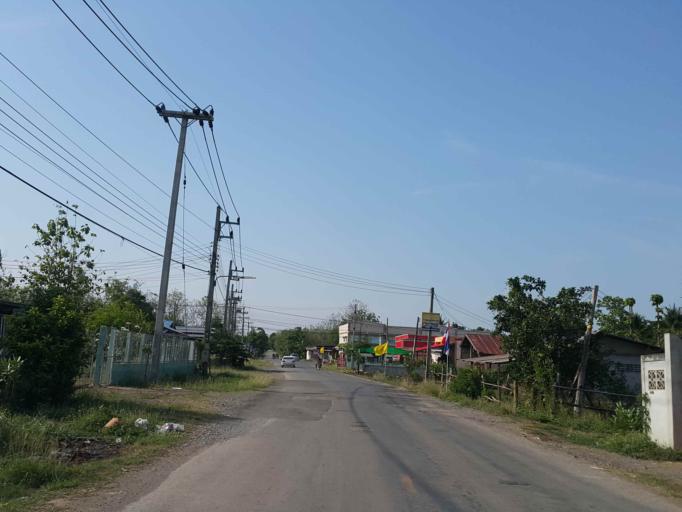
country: TH
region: Sukhothai
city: Thung Saliam
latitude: 17.3323
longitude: 99.5501
